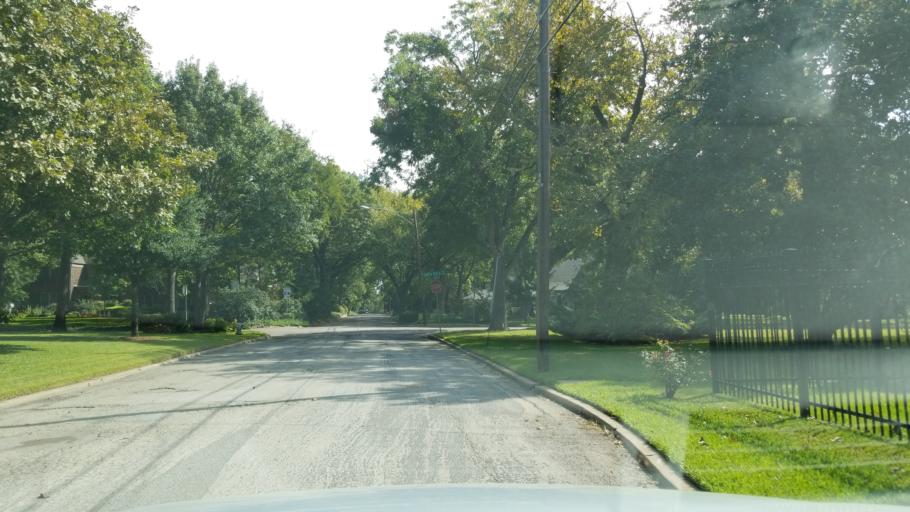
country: US
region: Texas
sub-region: Dallas County
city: Highland Park
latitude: 32.8119
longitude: -96.7183
